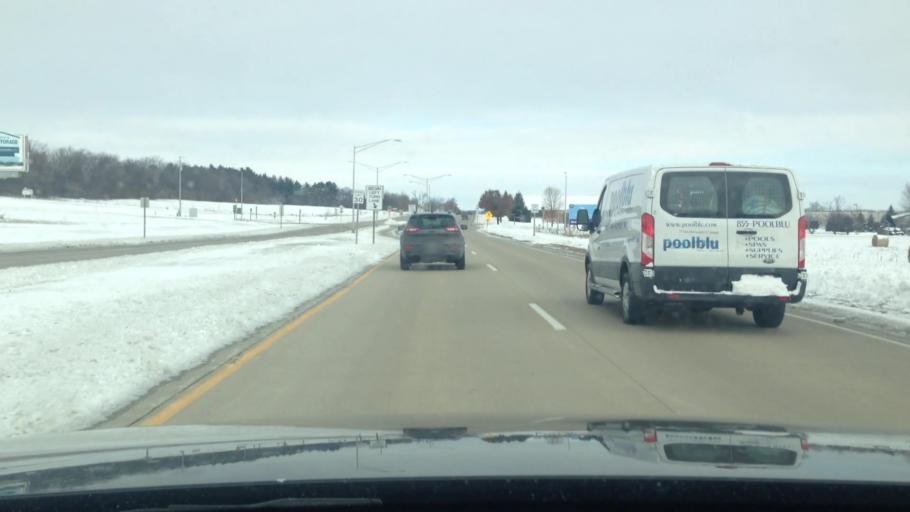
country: US
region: Wisconsin
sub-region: Walworth County
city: Lake Geneva
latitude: 42.5807
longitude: -88.4117
